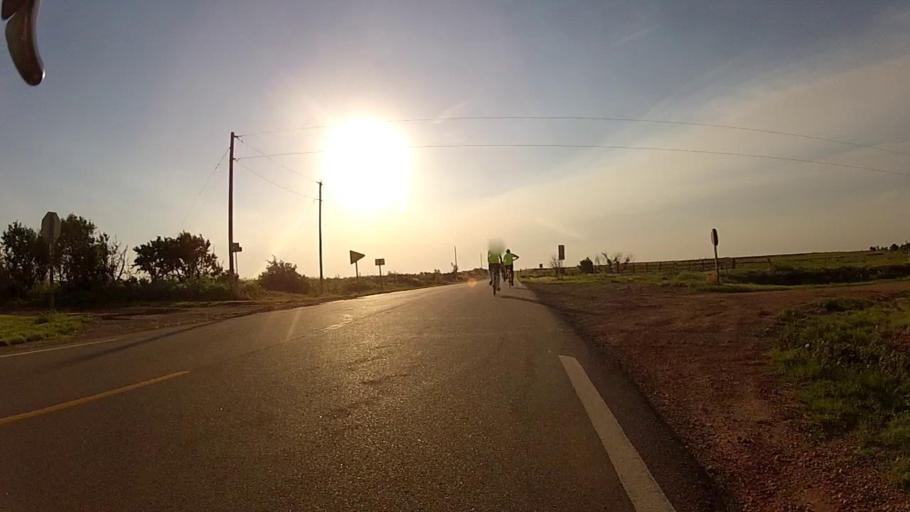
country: US
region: Kansas
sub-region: Harper County
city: Anthony
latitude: 37.1545
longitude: -97.8028
